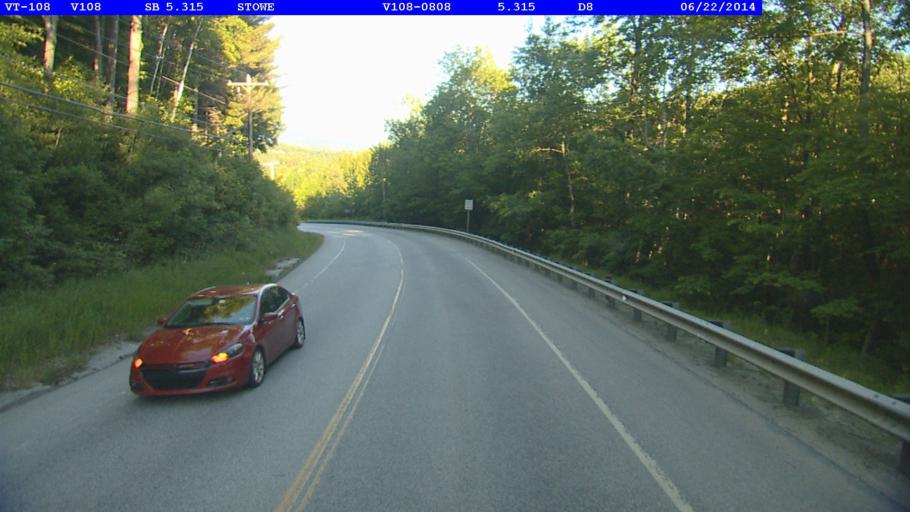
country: US
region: Vermont
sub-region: Lamoille County
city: Morristown
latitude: 44.5031
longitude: -72.7603
